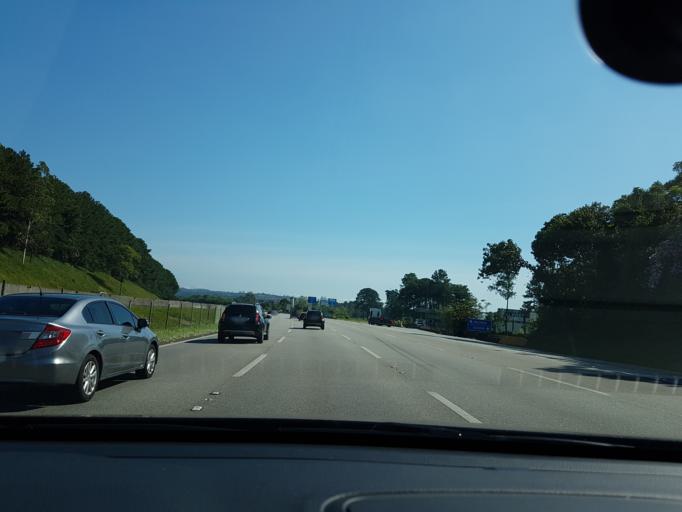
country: BR
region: Sao Paulo
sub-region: Sao Bernardo Do Campo
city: Sao Bernardo do Campo
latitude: -23.7799
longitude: -46.5972
